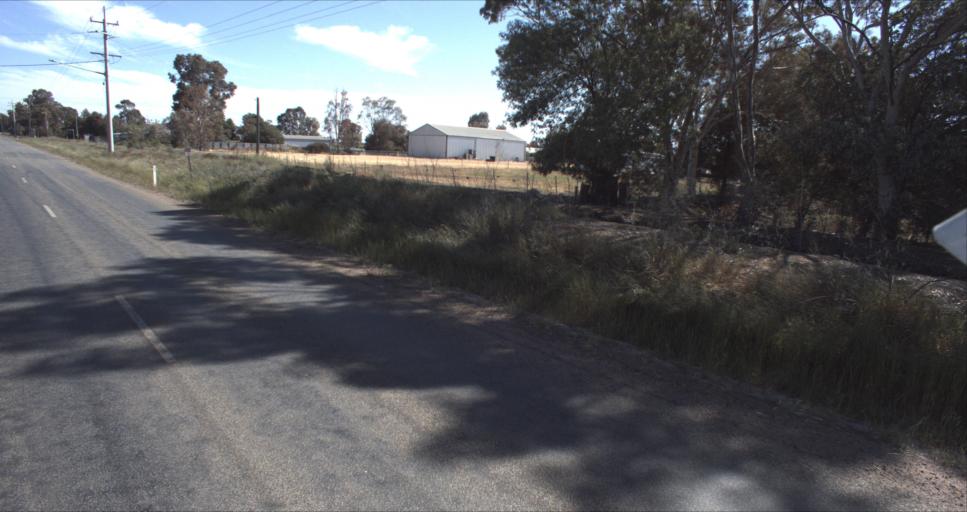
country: AU
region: New South Wales
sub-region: Leeton
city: Leeton
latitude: -34.5536
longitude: 146.3849
